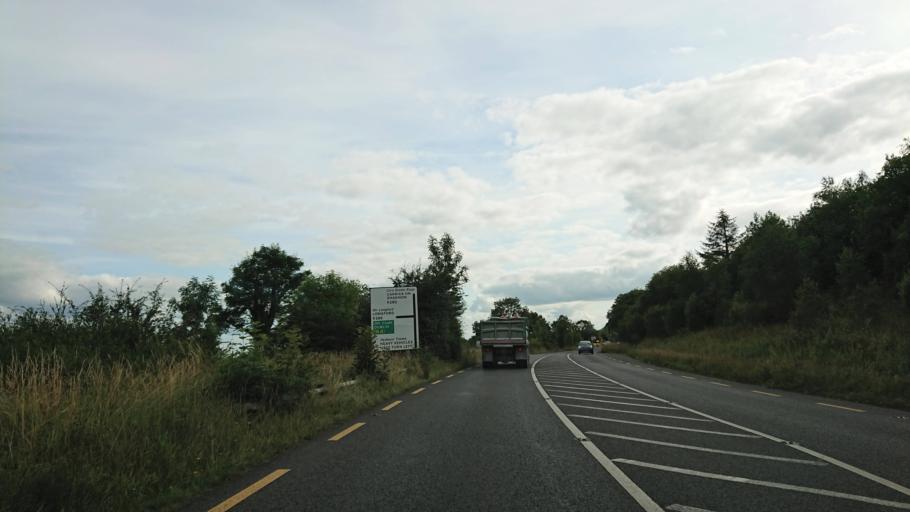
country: IE
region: Connaught
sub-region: County Leitrim
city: Carrick-on-Shannon
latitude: 53.9758
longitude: -8.0600
